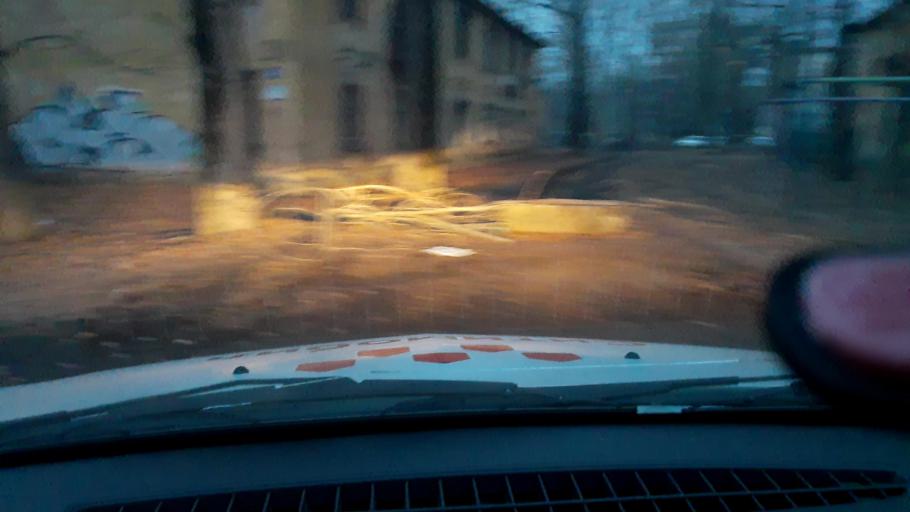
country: RU
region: Bashkortostan
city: Ufa
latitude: 54.7350
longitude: 55.9843
